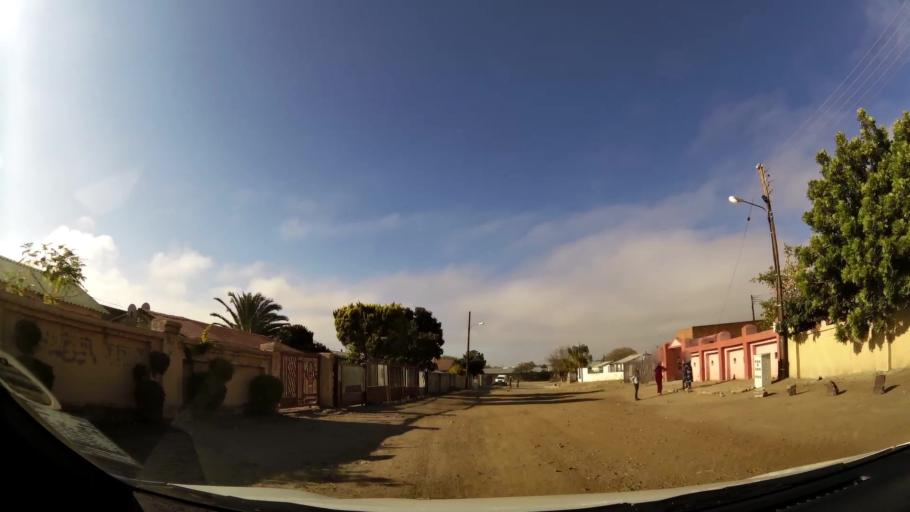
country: ZA
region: Limpopo
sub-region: Capricorn District Municipality
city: Polokwane
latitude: -23.8480
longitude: 29.3893
